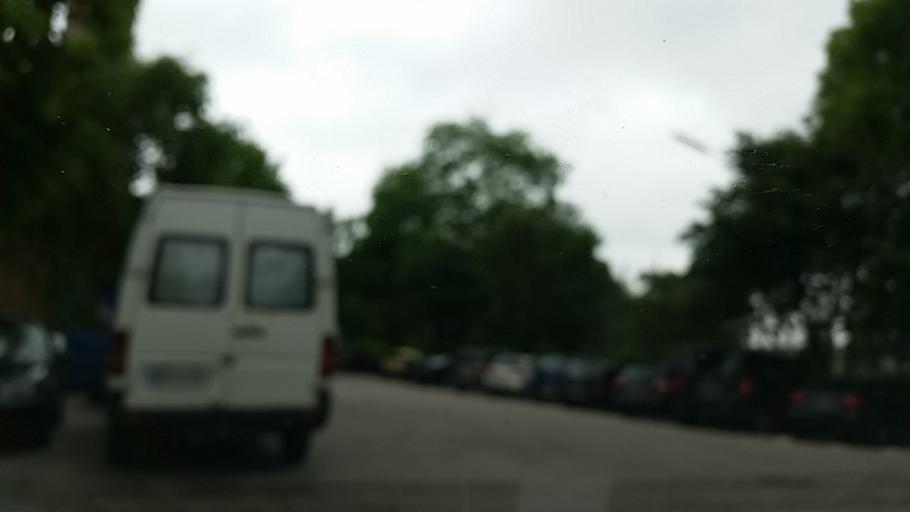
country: DE
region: Hamburg
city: Hammerbrook
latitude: 53.5260
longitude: 10.0178
